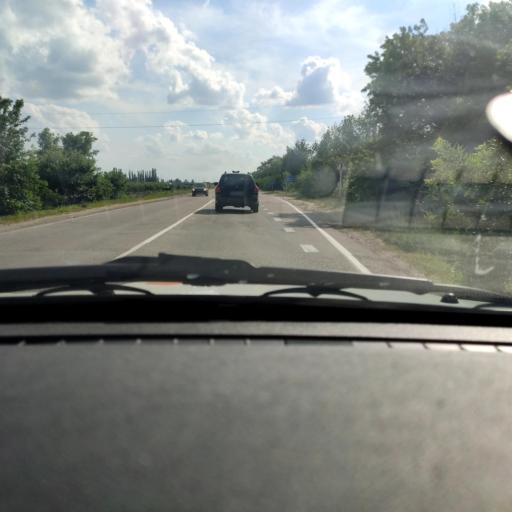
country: RU
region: Voronezj
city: Volya
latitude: 51.6944
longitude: 39.5034
